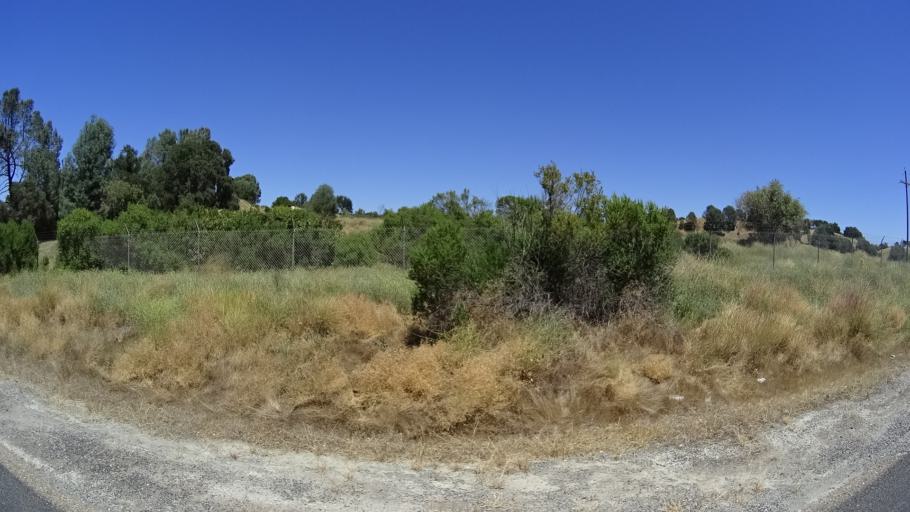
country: US
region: California
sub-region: Calaveras County
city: San Andreas
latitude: 38.1771
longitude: -120.6795
